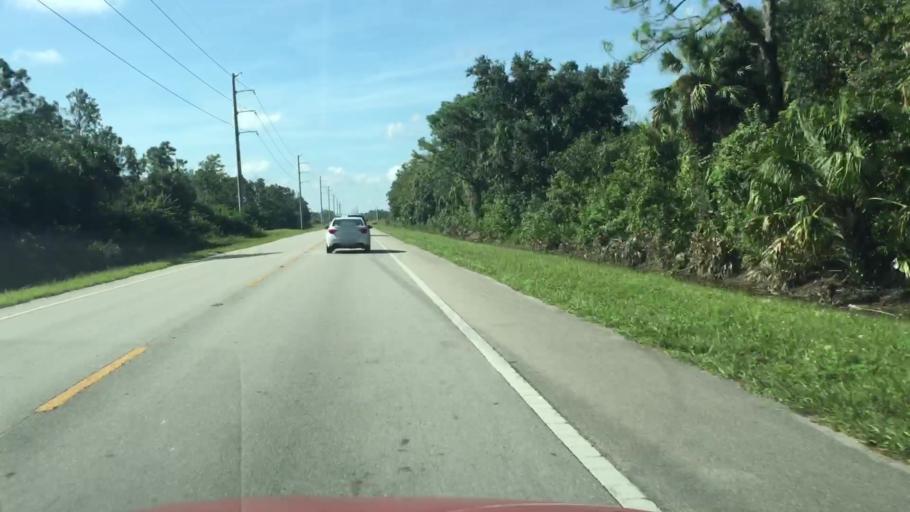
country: US
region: Florida
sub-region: Collier County
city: Orangetree
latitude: 26.3319
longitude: -81.5950
